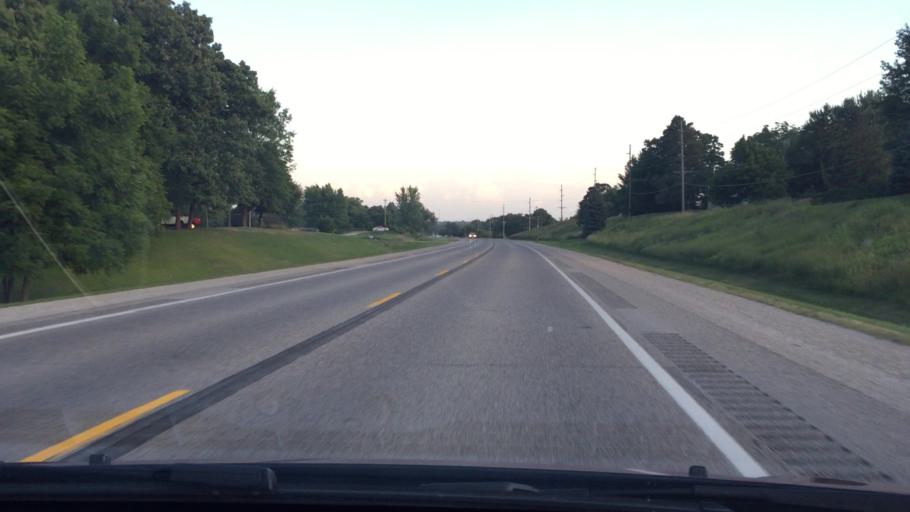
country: US
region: Iowa
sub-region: Muscatine County
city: Muscatine
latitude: 41.4741
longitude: -91.0379
